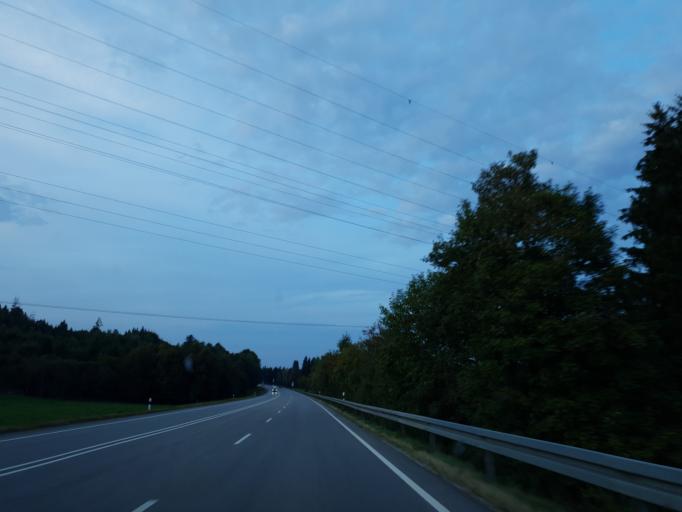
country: DE
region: Bavaria
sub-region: Swabia
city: Biessenhofen
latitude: 47.8239
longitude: 10.6713
